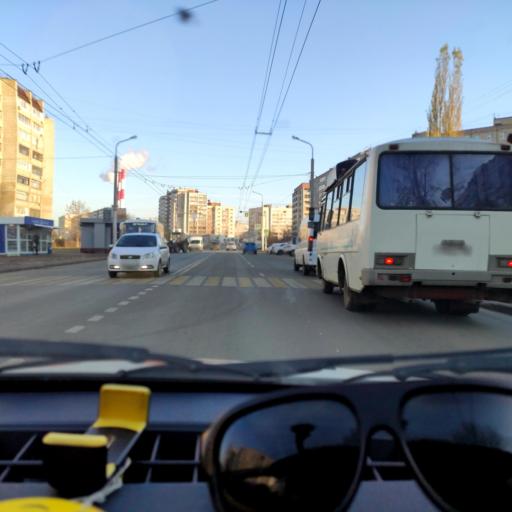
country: RU
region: Bashkortostan
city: Ufa
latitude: 54.7775
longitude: 56.1150
